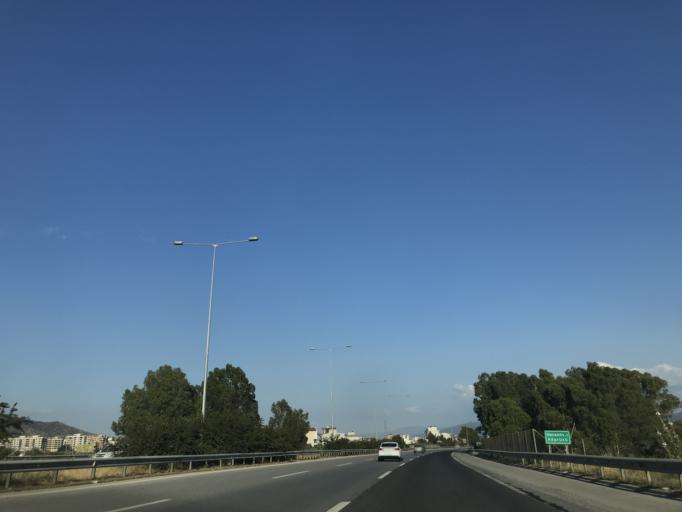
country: TR
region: Aydin
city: Aydin
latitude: 37.8585
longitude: 27.7969
